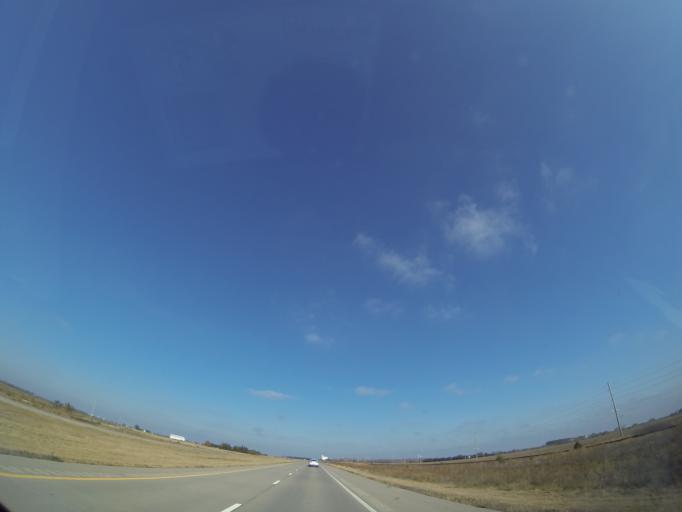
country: US
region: Kansas
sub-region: McPherson County
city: Inman
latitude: 38.2109
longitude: -97.7941
